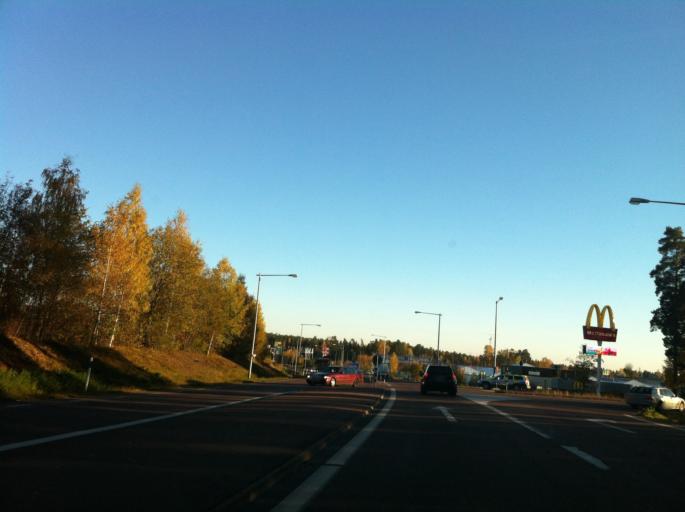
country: SE
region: Dalarna
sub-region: Faluns Kommun
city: Falun
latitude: 60.6101
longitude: 15.6545
